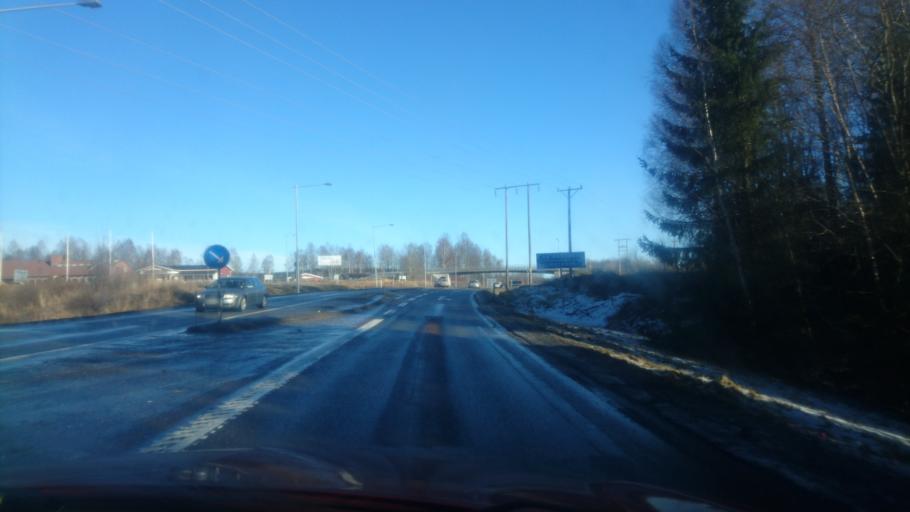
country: SE
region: Vaermland
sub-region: Sunne Kommun
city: Sunne
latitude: 59.7907
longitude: 13.0971
